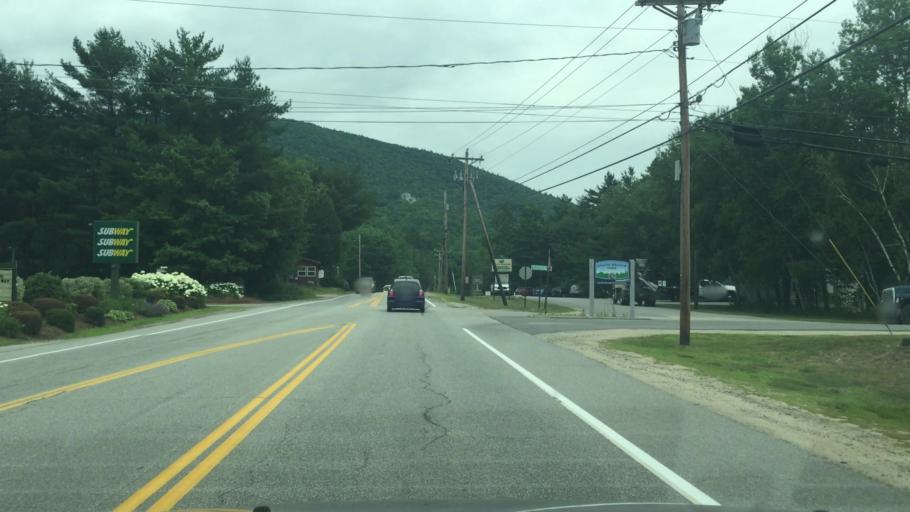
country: US
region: New Hampshire
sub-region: Carroll County
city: Center Harbor
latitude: 43.7226
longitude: -71.4317
